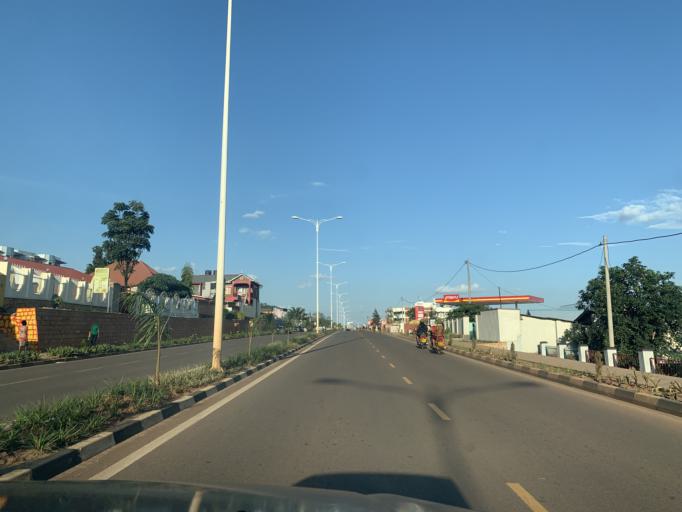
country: RW
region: Kigali
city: Kigali
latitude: -1.9619
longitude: 30.1109
